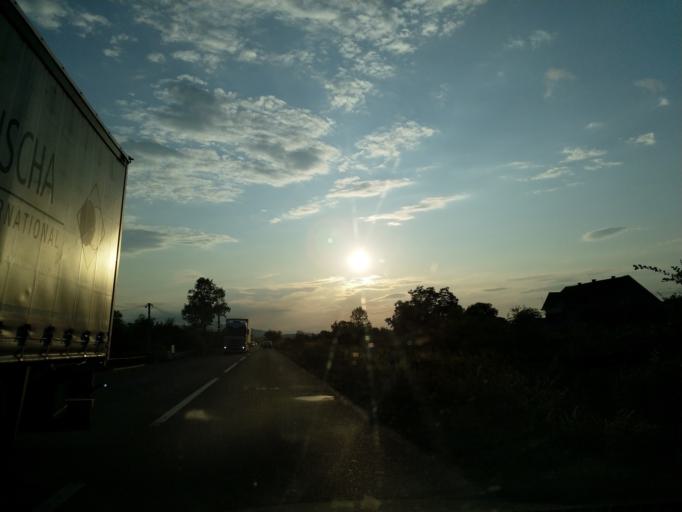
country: RS
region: Central Serbia
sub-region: Rasinski Okrug
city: Trstenik
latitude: 43.6329
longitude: 20.9588
